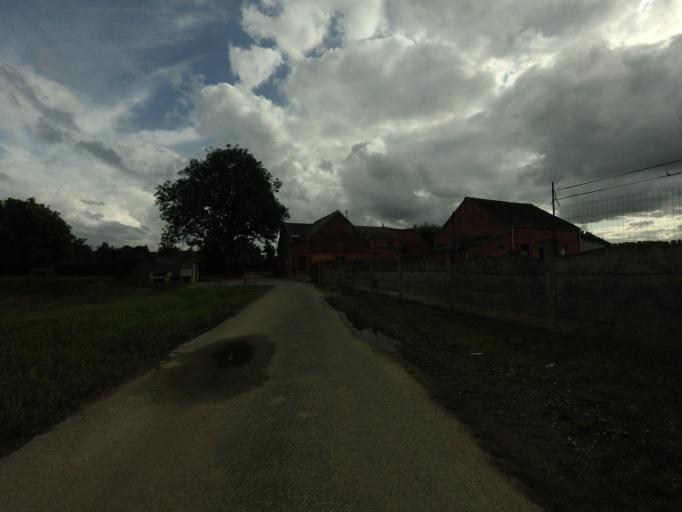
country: BE
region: Flanders
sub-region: Provincie Vlaams-Brabant
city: Kapelle-op-den-Bos
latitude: 51.0179
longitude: 4.3686
